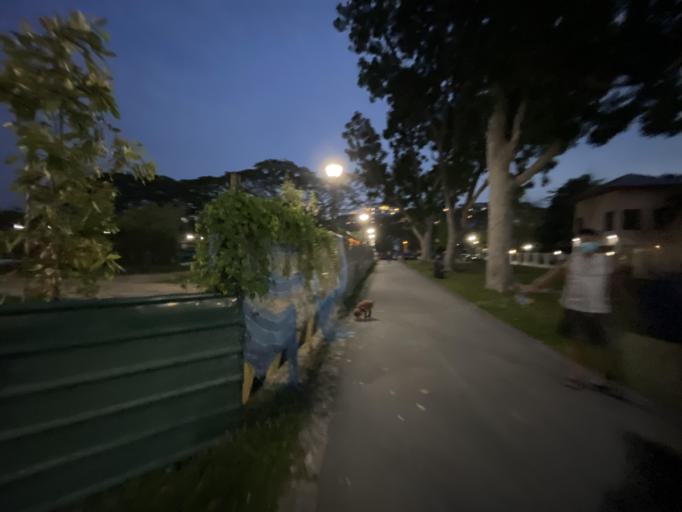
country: MY
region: Johor
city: Kampung Pasir Gudang Baru
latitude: 1.3804
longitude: 103.9595
